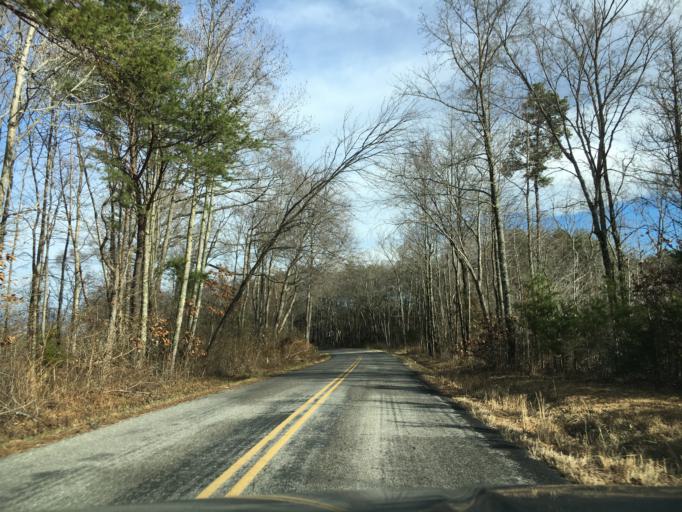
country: US
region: Virginia
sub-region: Nottoway County
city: Crewe
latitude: 37.3095
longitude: -78.1929
